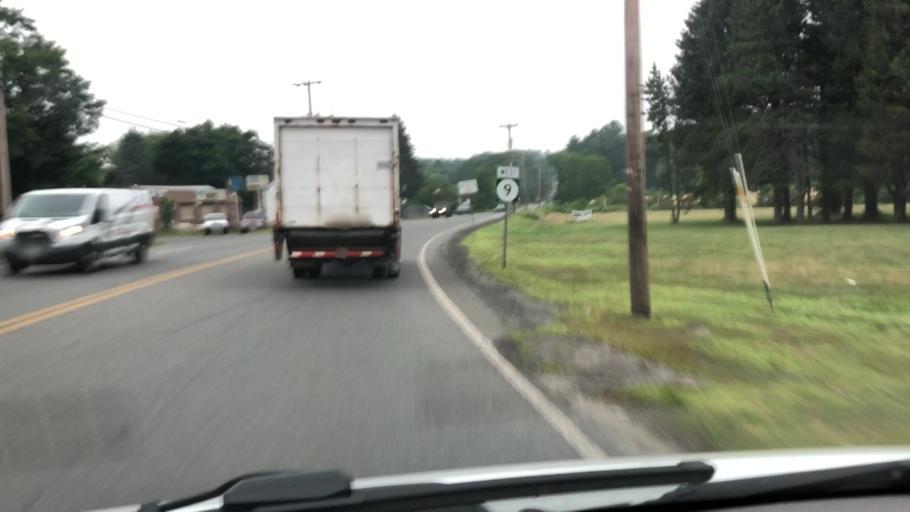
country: US
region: Massachusetts
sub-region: Hampshire County
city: Northampton
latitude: 42.3497
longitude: -72.6899
